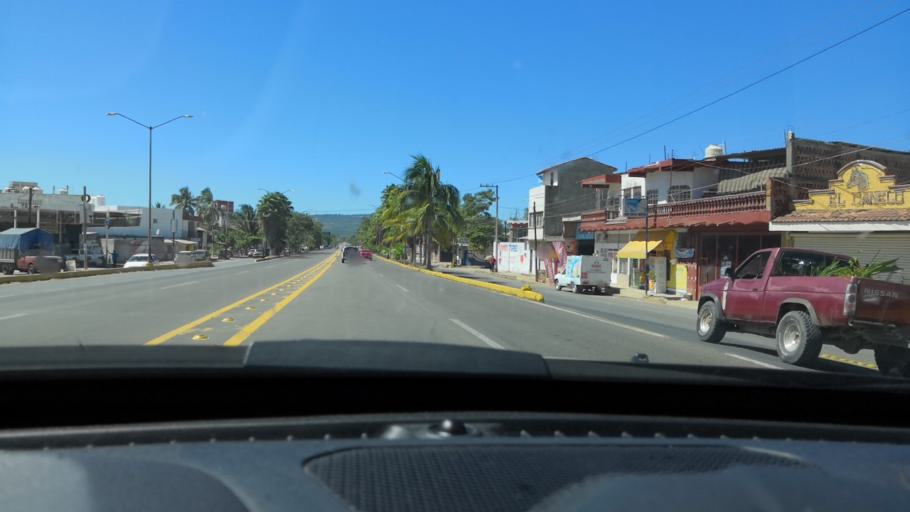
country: MX
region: Nayarit
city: Las Varas
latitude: 21.1812
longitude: -105.1337
